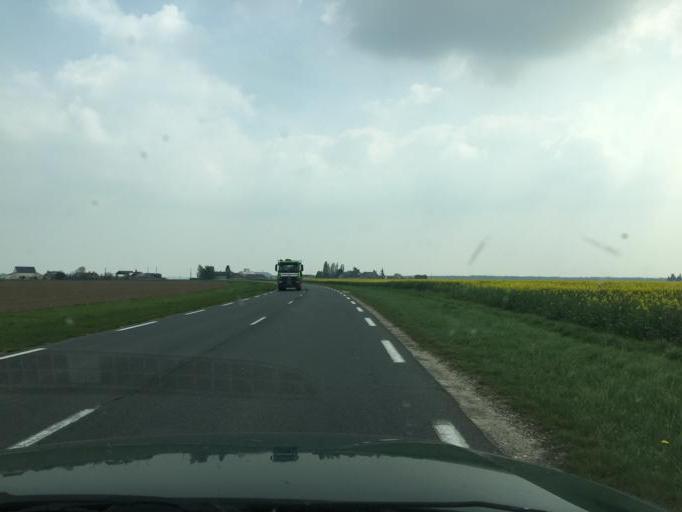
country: FR
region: Centre
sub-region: Departement du Loiret
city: Bricy
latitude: 47.9773
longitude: 1.7412
